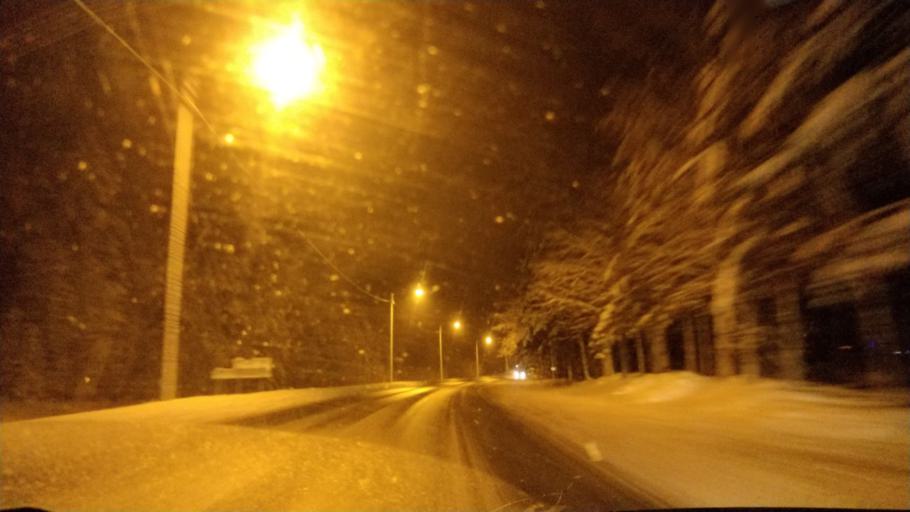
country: FI
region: Lapland
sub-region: Rovaniemi
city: Rovaniemi
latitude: 66.4354
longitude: 25.5251
